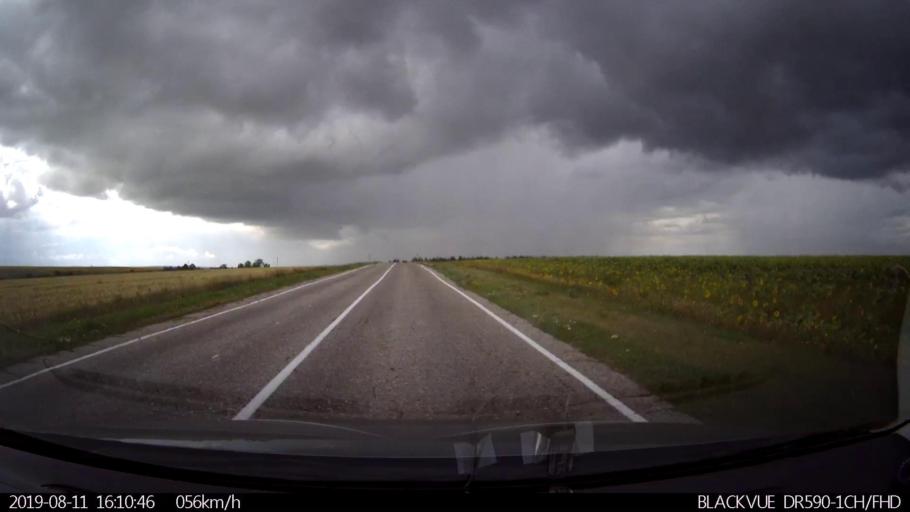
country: RU
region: Ulyanovsk
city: Ignatovka
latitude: 54.0000
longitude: 47.6513
